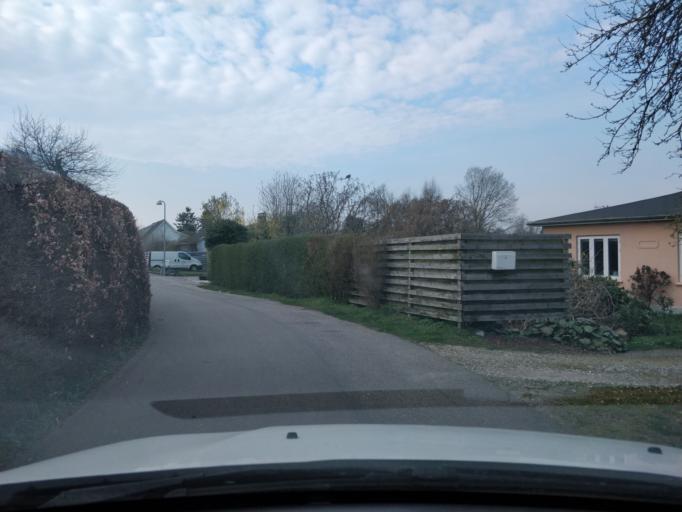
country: DK
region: Capital Region
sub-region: Hoje-Taastrup Kommune
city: Flong
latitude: 55.6508
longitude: 12.1905
